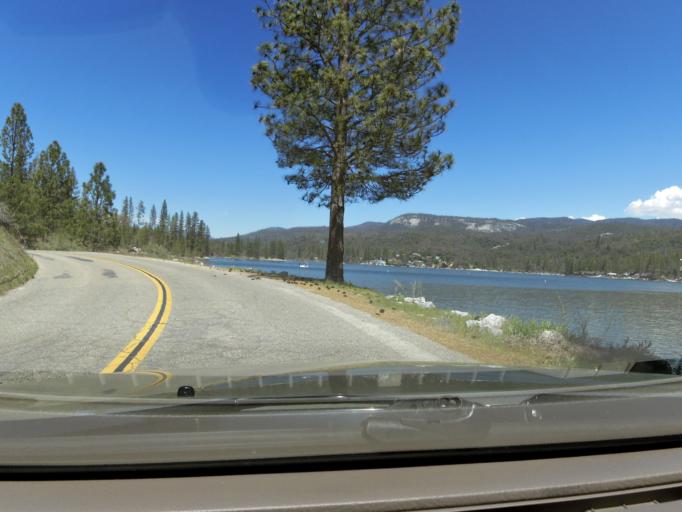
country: US
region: California
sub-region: Madera County
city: Oakhurst
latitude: 37.3187
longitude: -119.5757
